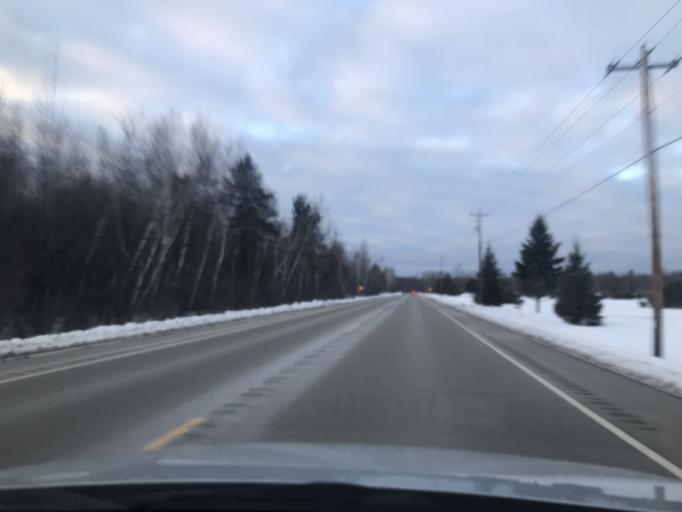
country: US
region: Wisconsin
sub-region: Marinette County
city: Marinette
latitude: 45.1362
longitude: -87.6897
